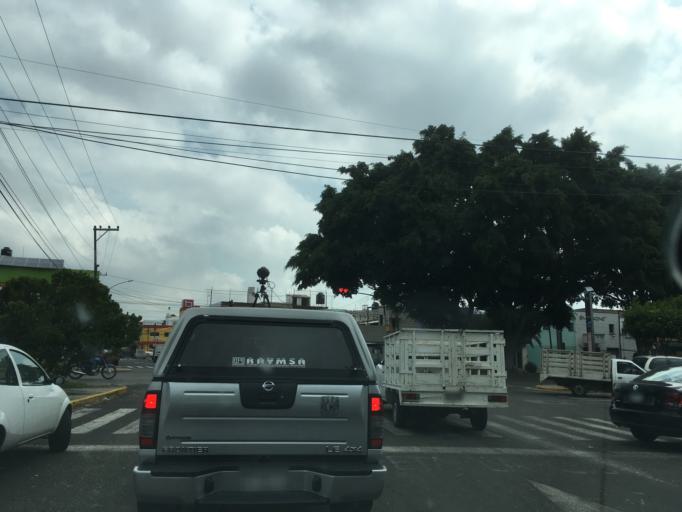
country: MX
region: Jalisco
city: Guadalajara
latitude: 20.6666
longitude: -103.3635
